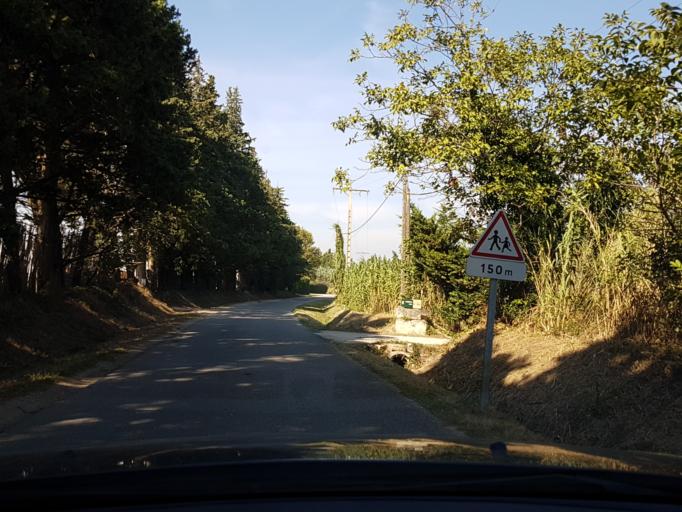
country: FR
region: Provence-Alpes-Cote d'Azur
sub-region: Departement des Bouches-du-Rhone
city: Eygalieres
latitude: 43.7760
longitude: 4.9336
